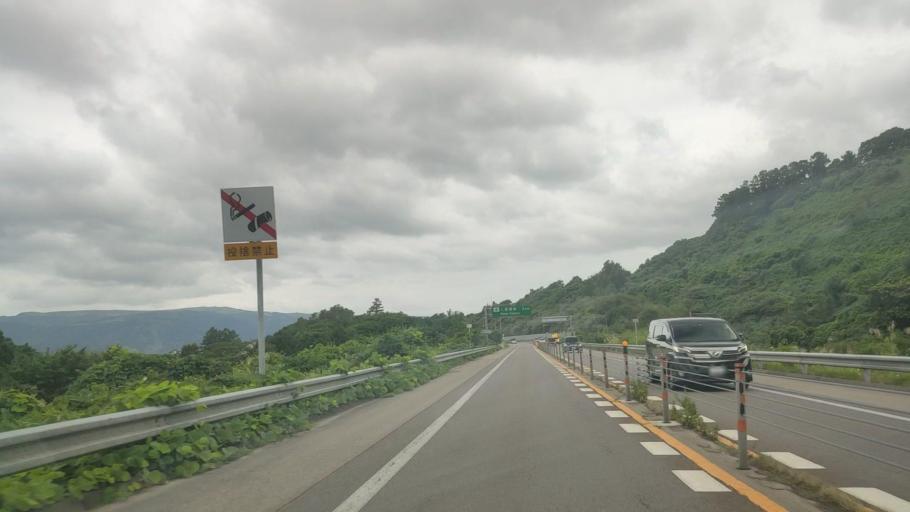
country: JP
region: Hokkaido
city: Nanae
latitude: 41.9122
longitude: 140.6921
